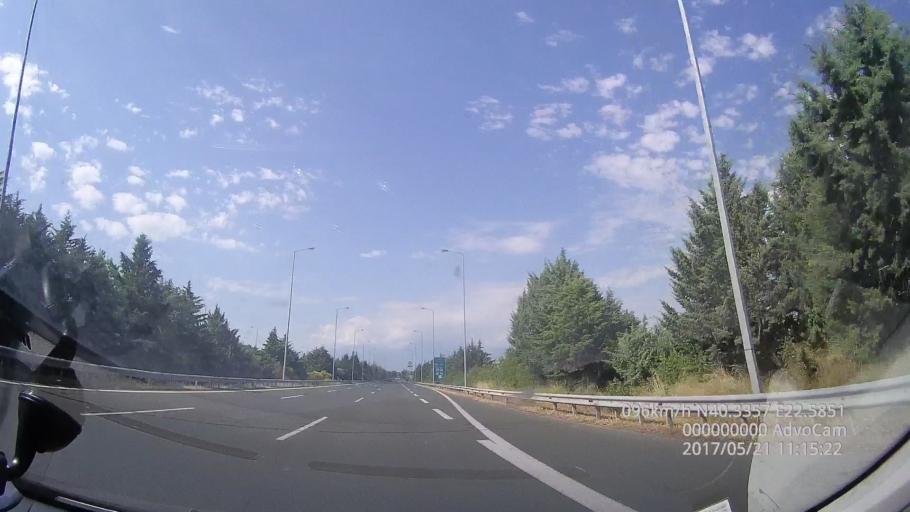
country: GR
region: Central Macedonia
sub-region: Nomos Pierias
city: Korinos
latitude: 40.3351
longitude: 22.5848
